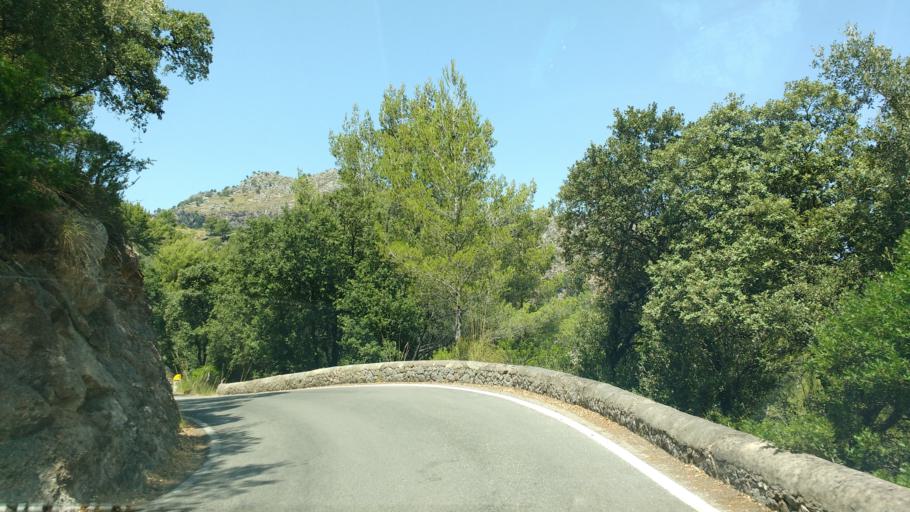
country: ES
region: Balearic Islands
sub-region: Illes Balears
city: Escorca
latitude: 39.8382
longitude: 2.7979
